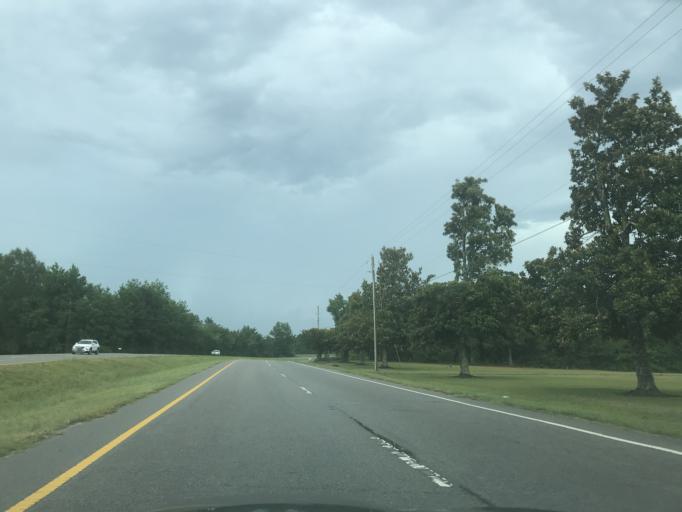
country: US
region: North Carolina
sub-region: Johnston County
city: Wilsons Mills
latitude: 35.5719
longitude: -78.3952
